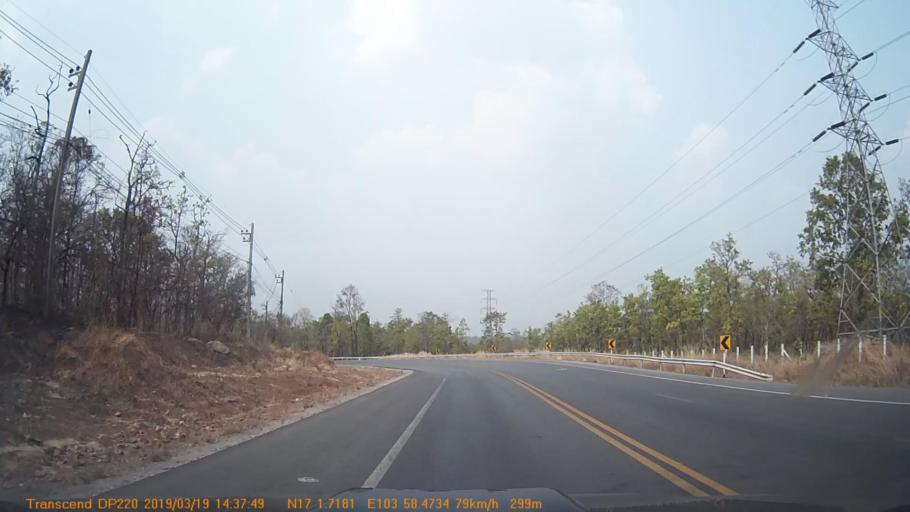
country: TH
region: Sakon Nakhon
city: Phu Phan
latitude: 17.0289
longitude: 103.9746
